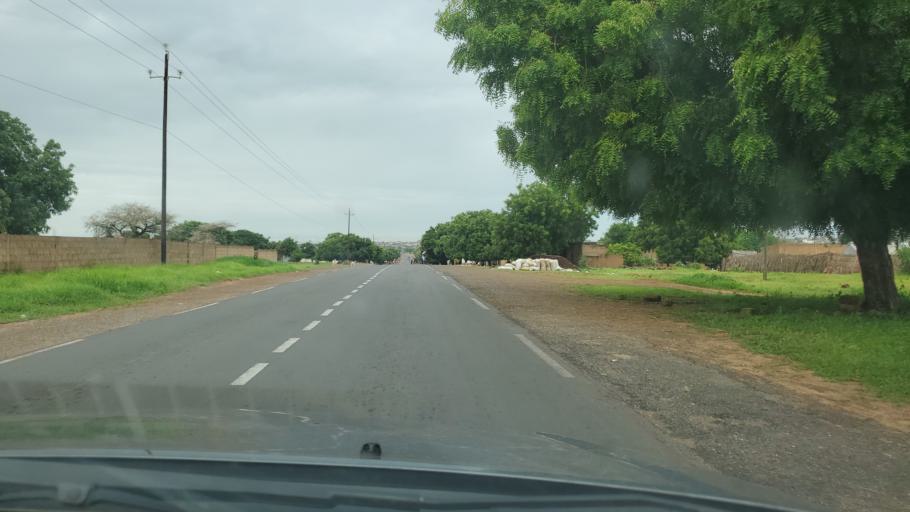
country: SN
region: Thies
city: Mekhe
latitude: 15.1323
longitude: -16.8582
